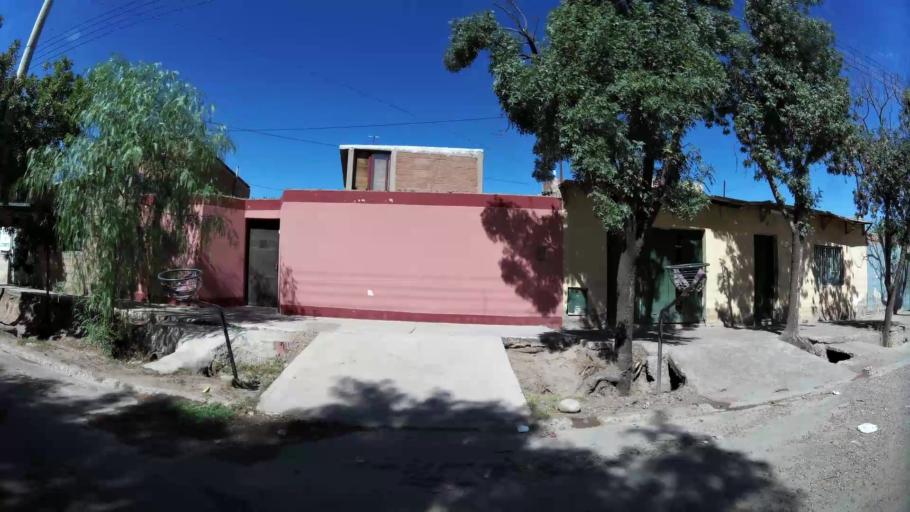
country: AR
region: Mendoza
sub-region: Departamento de Godoy Cruz
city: Godoy Cruz
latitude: -32.9598
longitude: -68.8329
